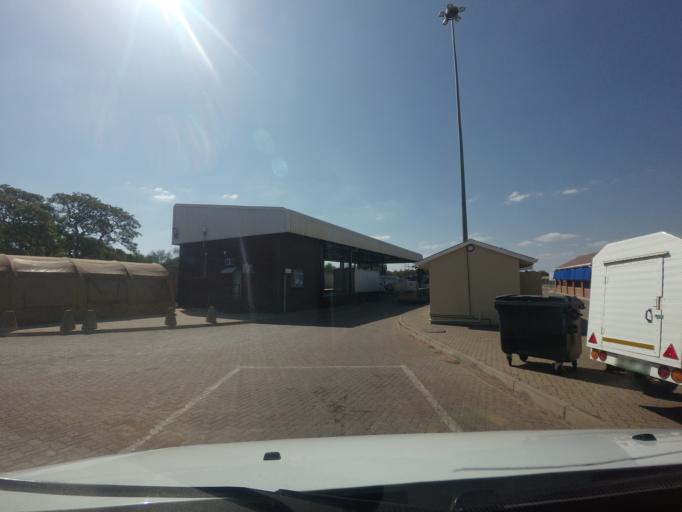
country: BW
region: Central
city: Makobeng
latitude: -22.9997
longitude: 27.9439
